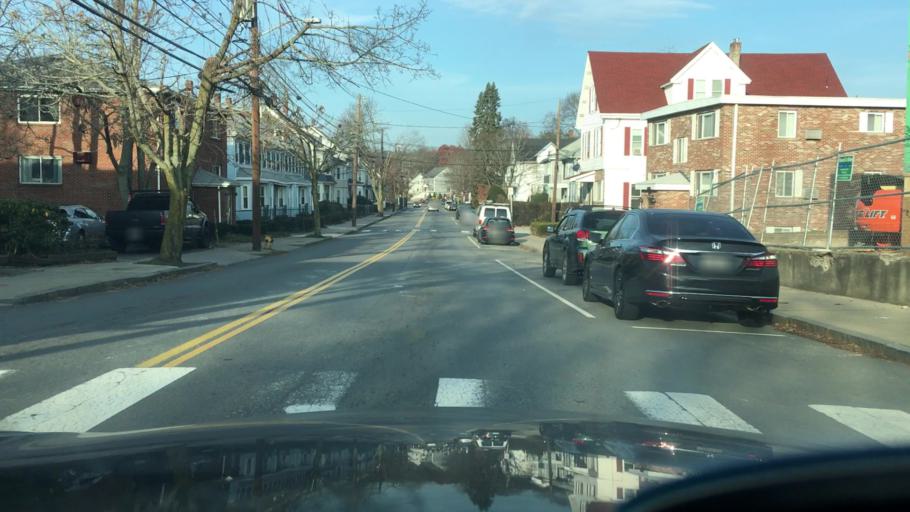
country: US
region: Massachusetts
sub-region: Middlesex County
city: Waltham
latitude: 42.3721
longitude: -71.2255
